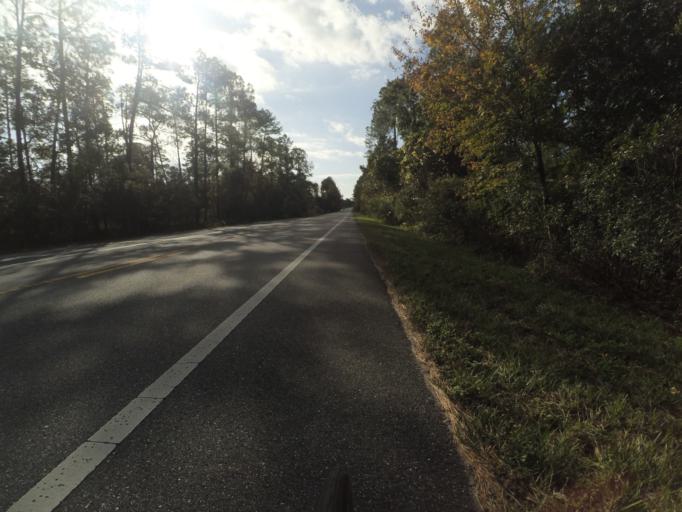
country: US
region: Florida
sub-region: Lake County
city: Astor
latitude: 29.1161
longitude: -81.6178
